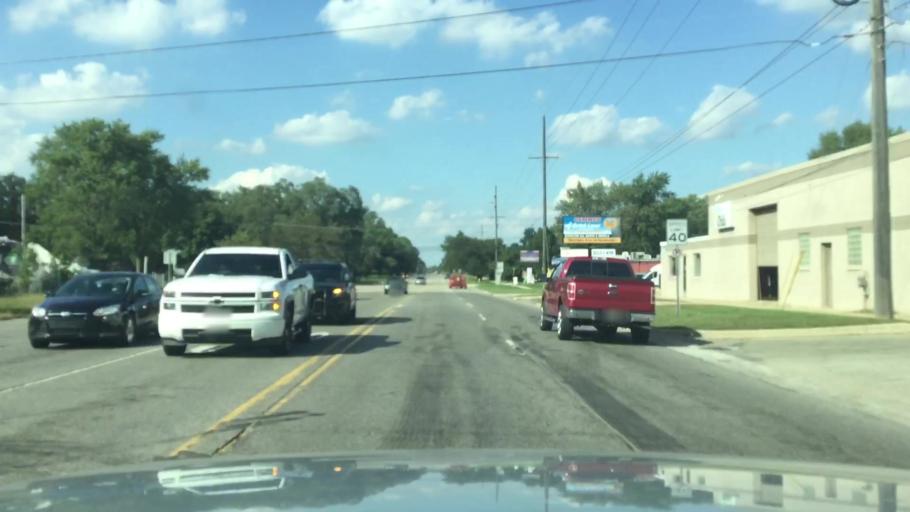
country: US
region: Michigan
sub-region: Wayne County
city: Westland
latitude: 42.3244
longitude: -83.4086
